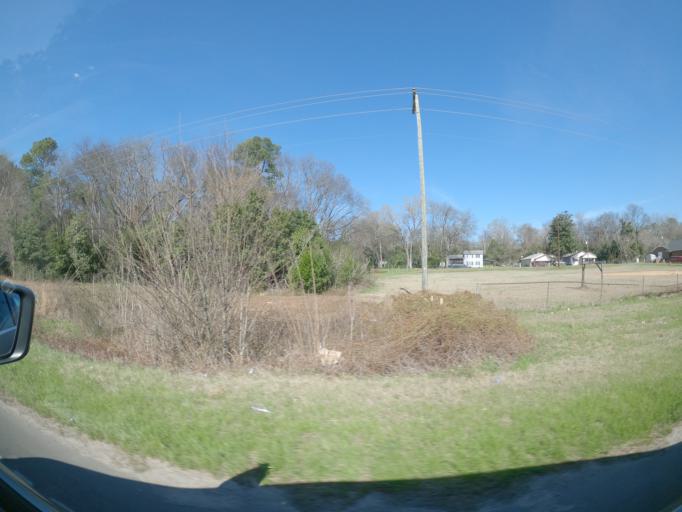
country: US
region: South Carolina
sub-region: Aiken County
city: Warrenville
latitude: 33.5557
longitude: -81.8057
